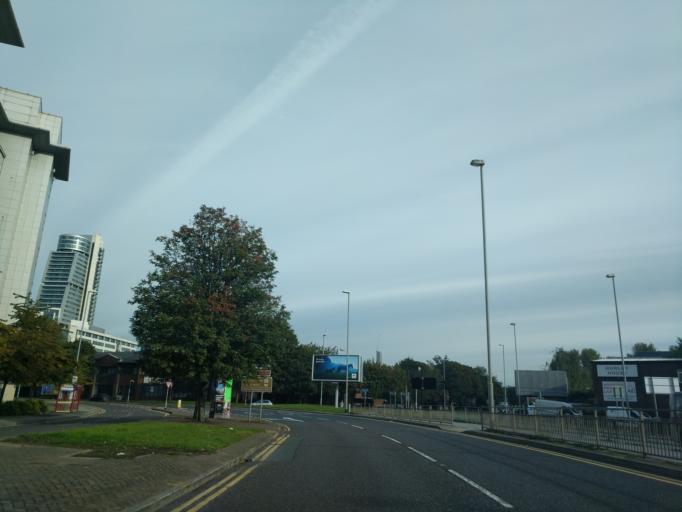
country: GB
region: England
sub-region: City and Borough of Leeds
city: Leeds
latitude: 53.7886
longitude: -1.5458
